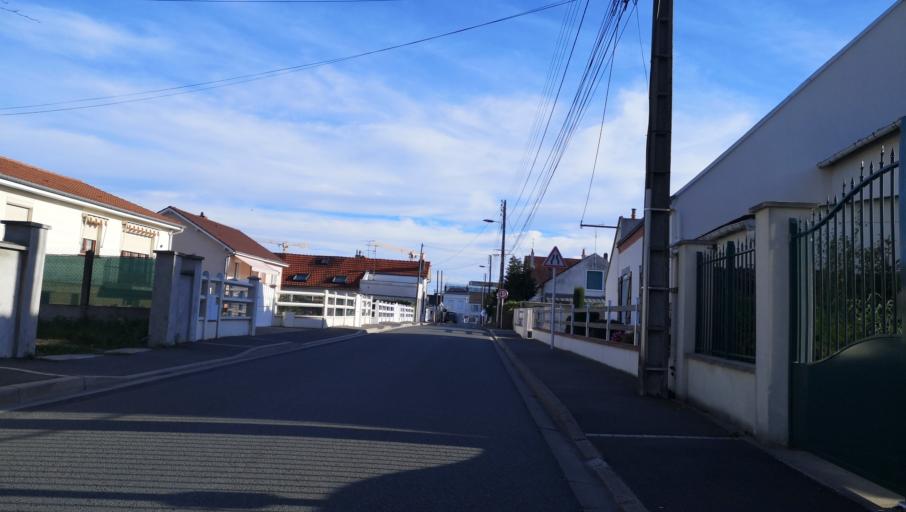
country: FR
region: Centre
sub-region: Departement du Loiret
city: Fleury-les-Aubrais
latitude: 47.9243
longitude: 1.9228
